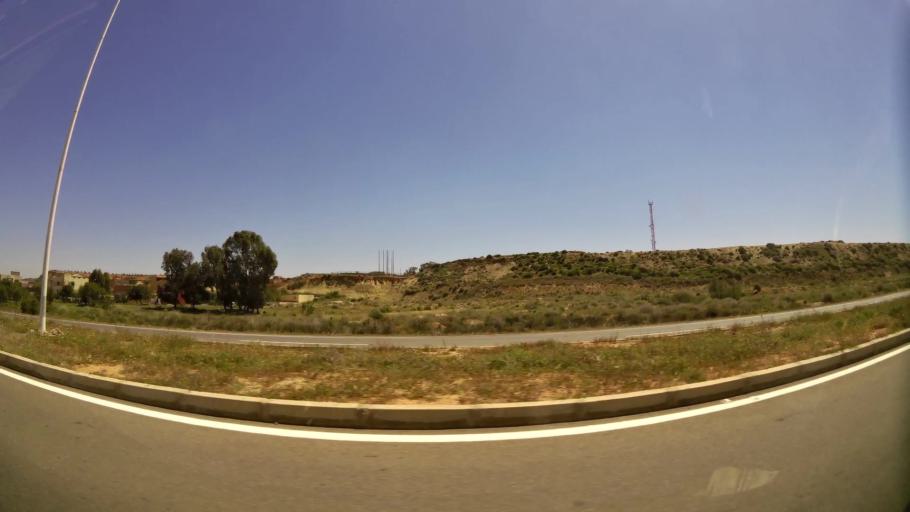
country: MA
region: Oriental
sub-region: Berkane-Taourirt
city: Madagh
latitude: 35.1000
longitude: -2.3256
